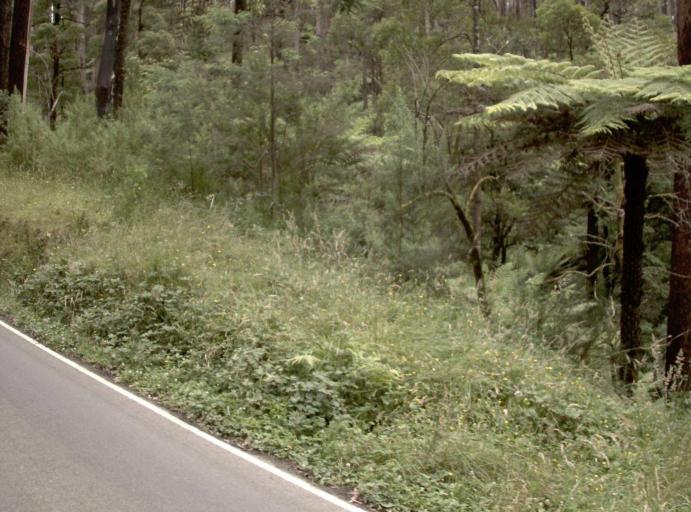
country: AU
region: Victoria
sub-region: Yarra Ranges
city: Healesville
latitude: -37.5917
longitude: 145.6395
